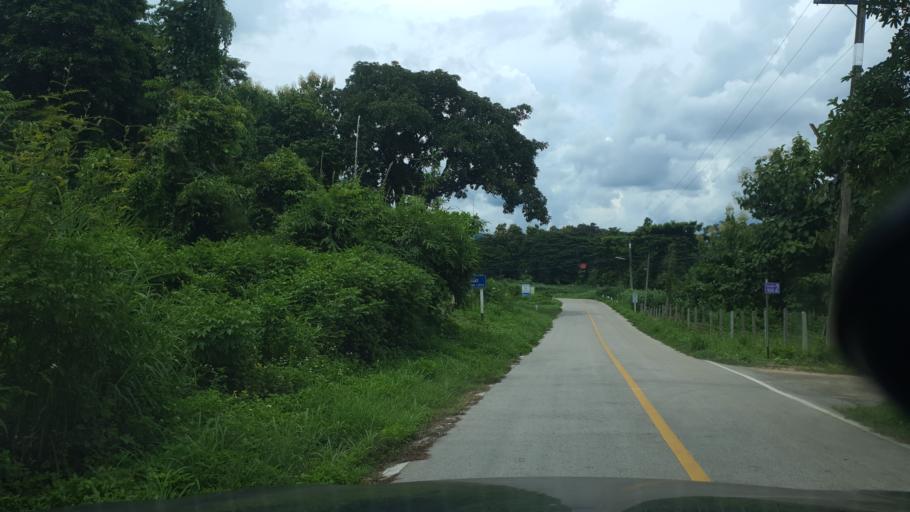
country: TH
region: Lampang
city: Hang Chat
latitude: 18.4004
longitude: 99.2630
